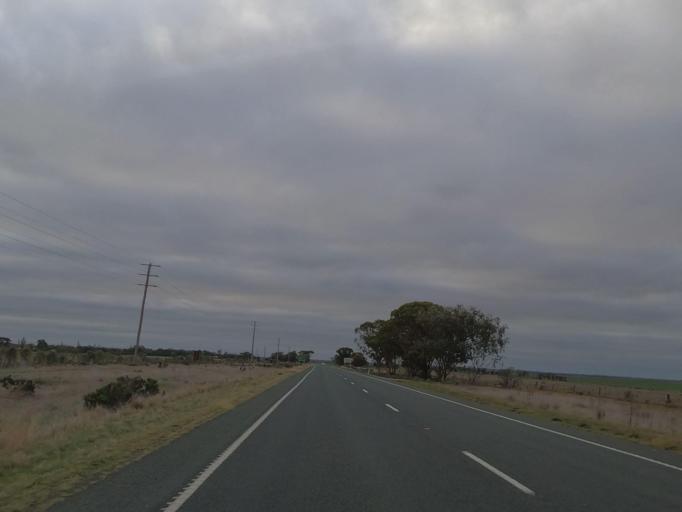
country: AU
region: Victoria
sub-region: Swan Hill
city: Swan Hill
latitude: -35.5692
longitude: 143.7853
